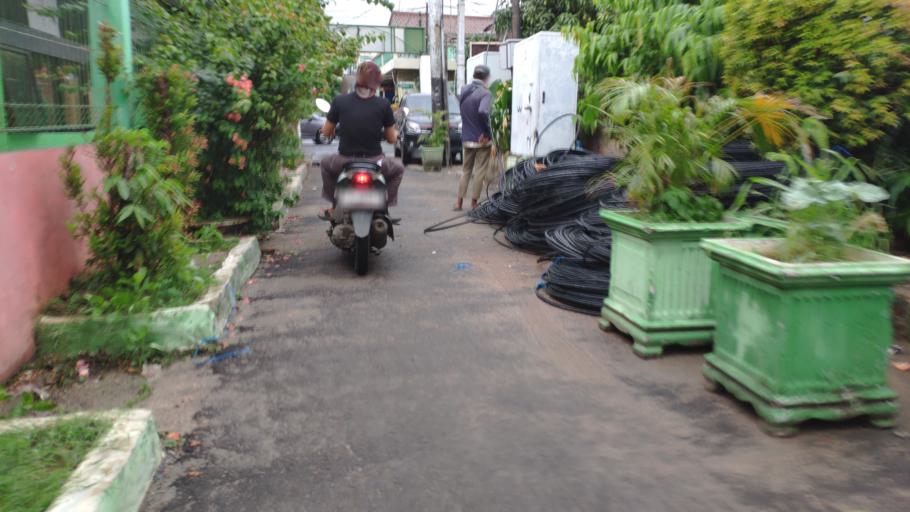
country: ID
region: Jakarta Raya
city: Jakarta
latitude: -6.2045
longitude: 106.8674
